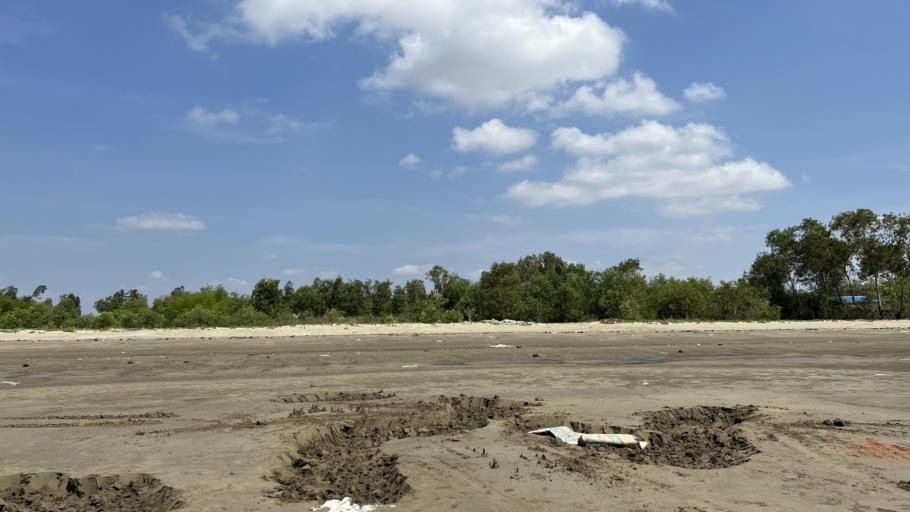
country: MM
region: Ayeyarwady
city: Pyapon
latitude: 15.8984
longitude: 95.6155
